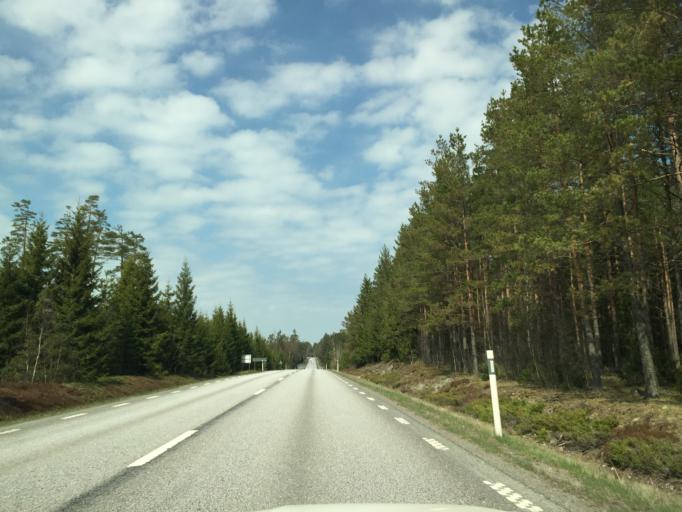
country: SE
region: Vaestra Goetaland
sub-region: Bengtsfors Kommun
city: Dals Langed
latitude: 58.8126
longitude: 12.1458
